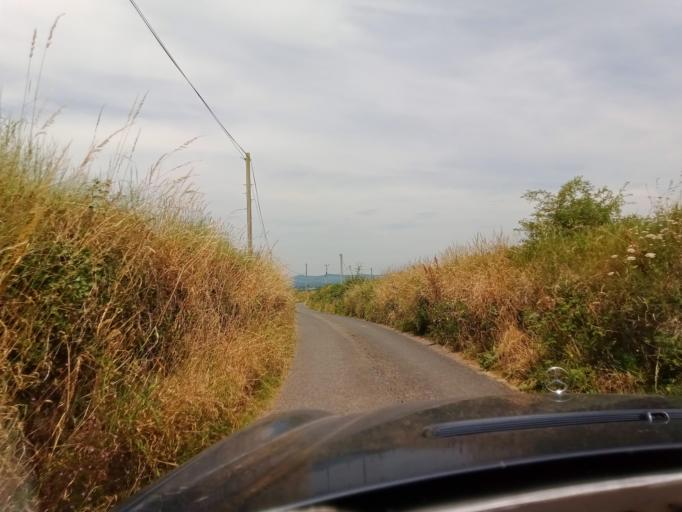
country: IE
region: Leinster
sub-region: Kilkenny
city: Mooncoin
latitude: 52.2655
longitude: -7.2153
